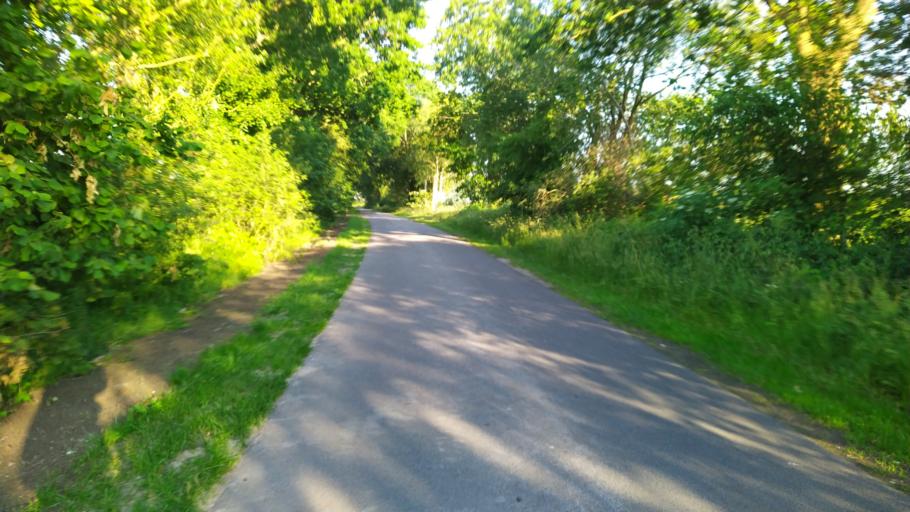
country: DE
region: Lower Saxony
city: Alfstedt
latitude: 53.5581
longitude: 9.0386
